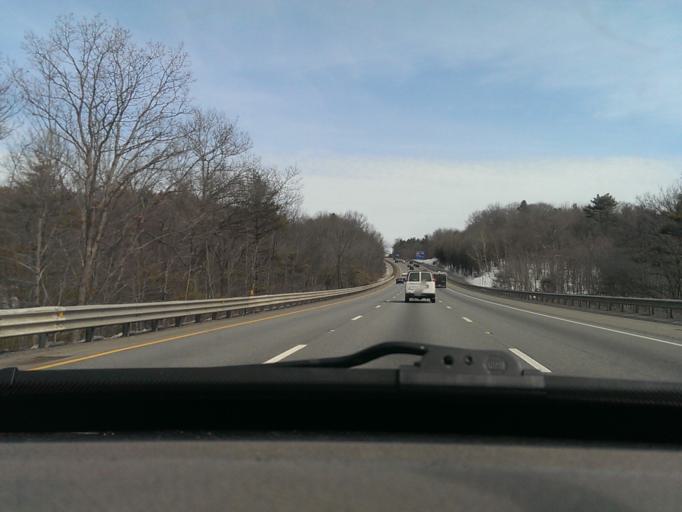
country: US
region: Massachusetts
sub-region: Worcester County
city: Sturbridge
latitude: 42.1362
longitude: -72.0378
